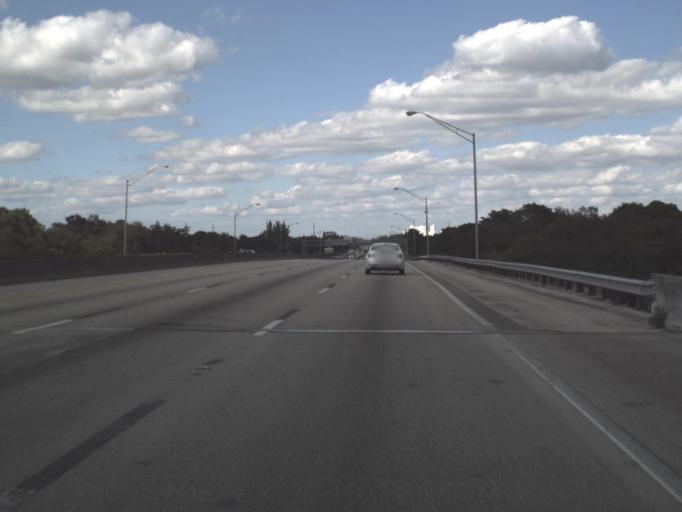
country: US
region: Florida
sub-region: Broward County
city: Pembroke Pines
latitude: 26.0249
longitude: -80.2130
